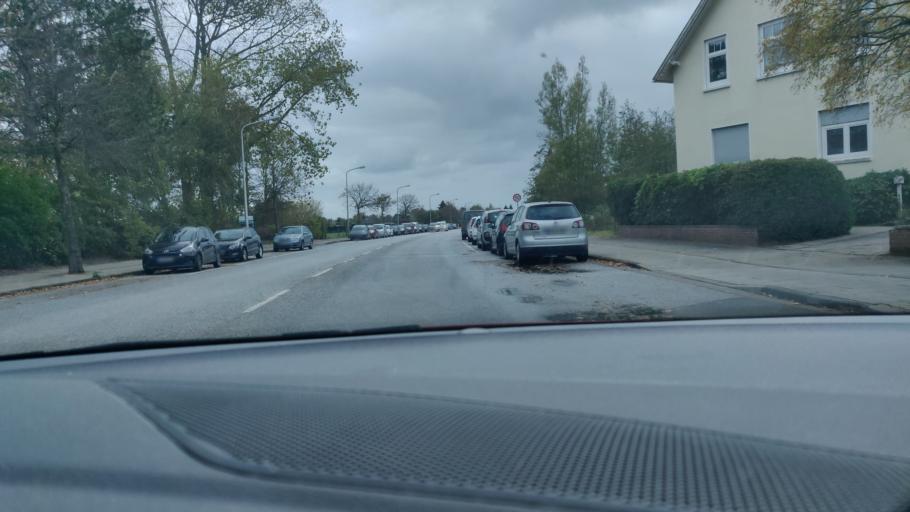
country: DE
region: Lower Saxony
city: Cuxhaven
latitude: 53.8809
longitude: 8.6726
